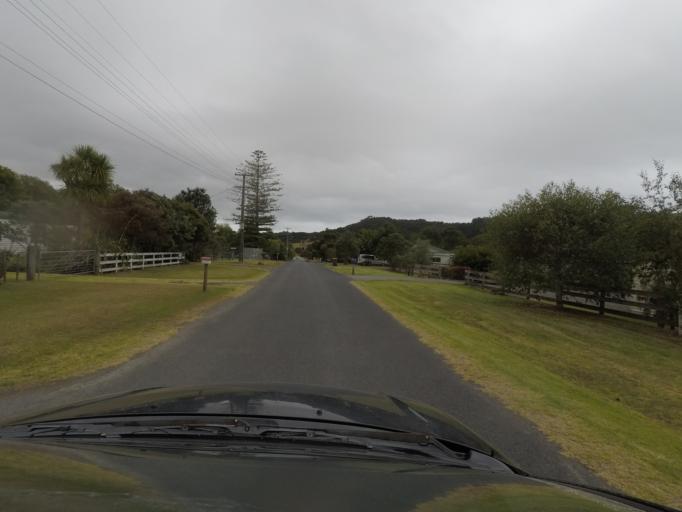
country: NZ
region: Auckland
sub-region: Auckland
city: Warkworth
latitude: -36.2660
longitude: 174.7279
